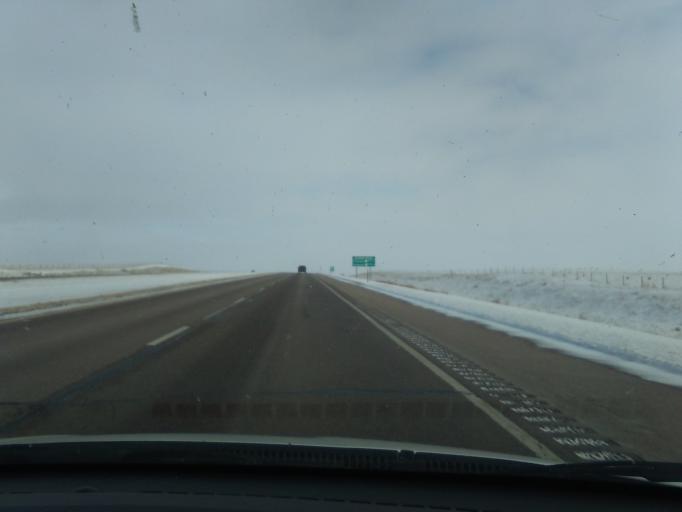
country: US
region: Nebraska
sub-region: Kimball County
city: Kimball
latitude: 41.2112
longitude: -103.6979
